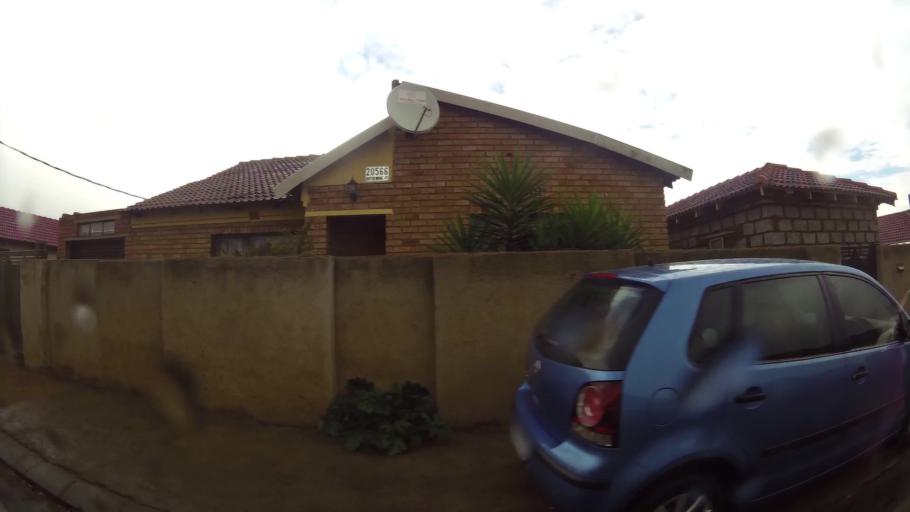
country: ZA
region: Gauteng
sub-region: Ekurhuleni Metropolitan Municipality
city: Germiston
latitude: -26.3403
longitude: 28.2081
